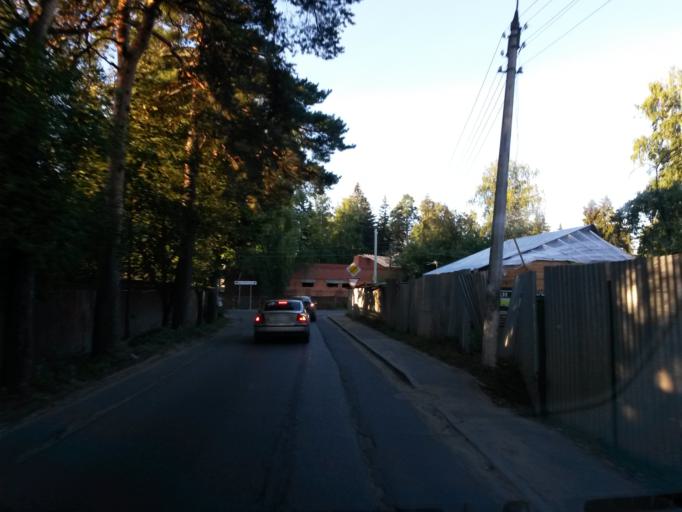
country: RU
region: Moskovskaya
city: Mamontovka
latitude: 55.9801
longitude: 37.8426
